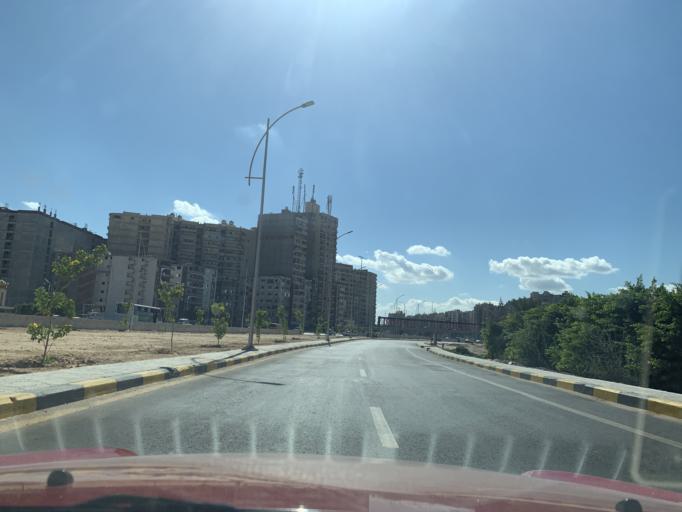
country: EG
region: Alexandria
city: Alexandria
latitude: 31.2128
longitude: 29.9609
